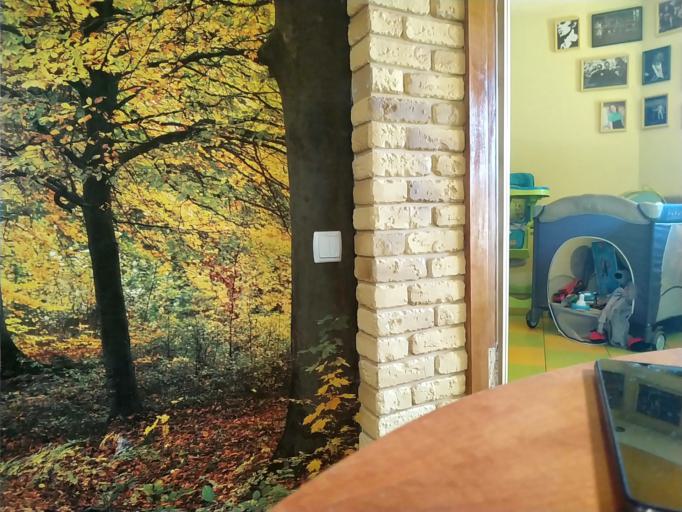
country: RU
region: Tverskaya
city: Krasnomayskiy
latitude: 57.5290
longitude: 34.1685
